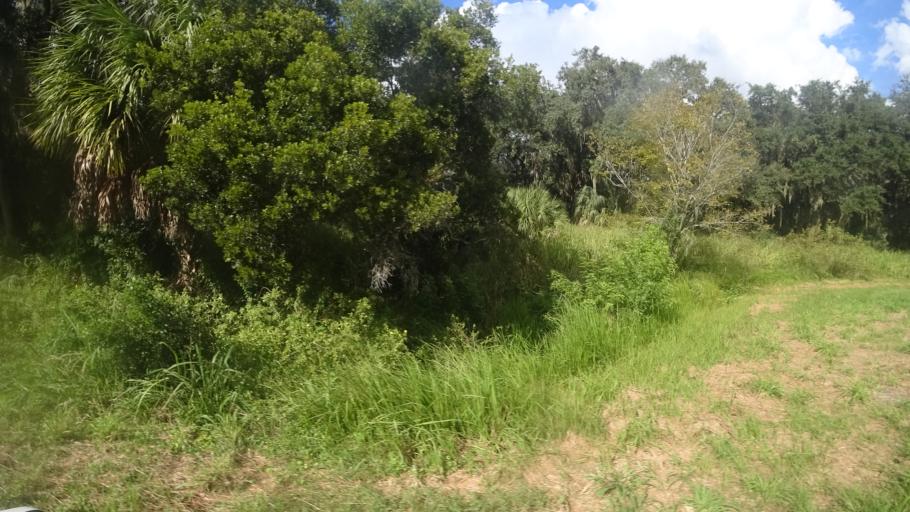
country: US
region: Florida
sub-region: Manatee County
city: Memphis
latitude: 27.6014
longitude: -82.5415
